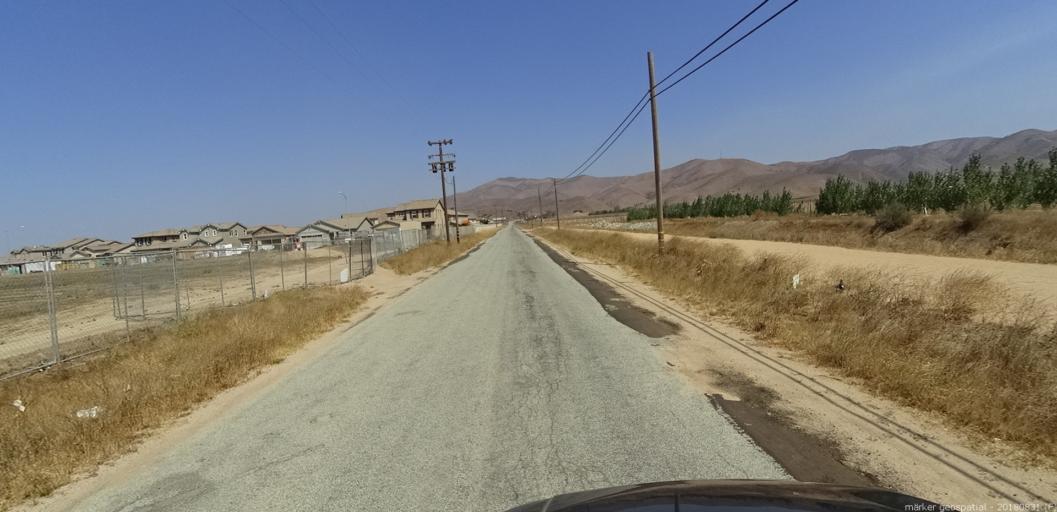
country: US
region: California
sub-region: Monterey County
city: Soledad
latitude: 36.4362
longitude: -121.3117
